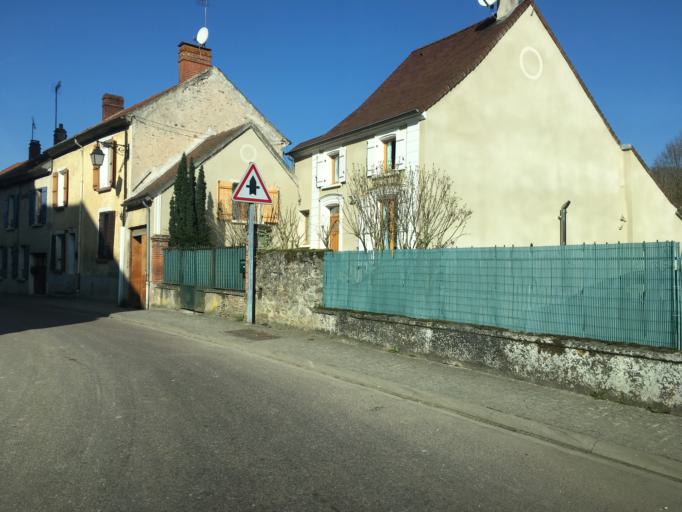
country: FR
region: Picardie
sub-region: Departement de l'Aisne
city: Chateau-Thierry
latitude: 49.1083
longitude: 3.3483
